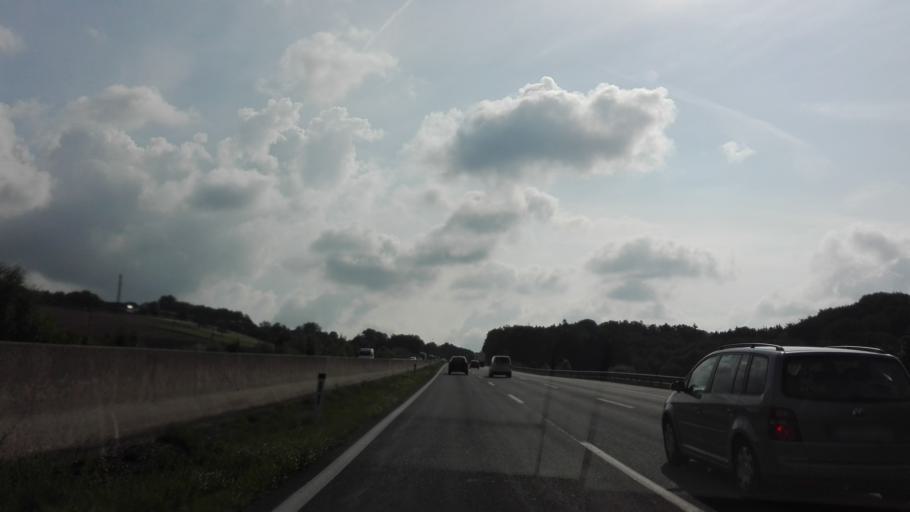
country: AT
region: Lower Austria
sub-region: Politischer Bezirk Amstetten
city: Sankt Georgen am Ybbsfelde
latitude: 48.1383
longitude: 14.9379
